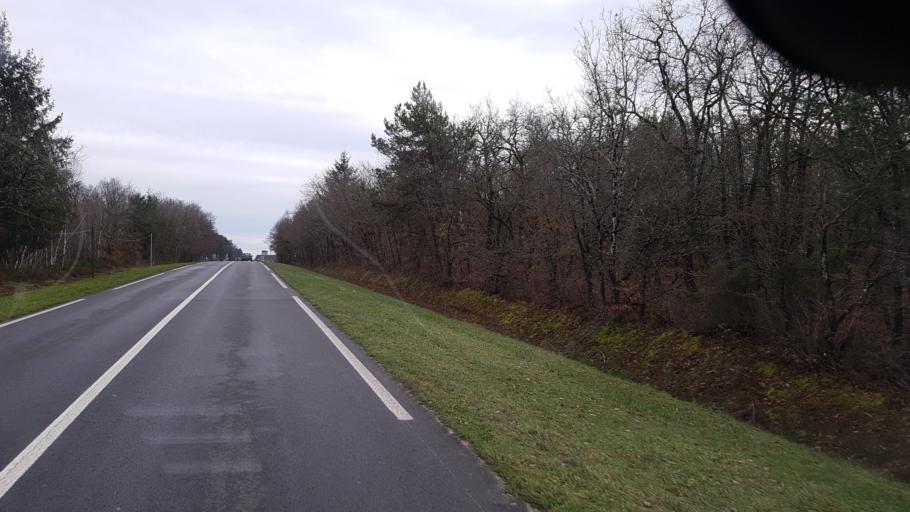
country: FR
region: Centre
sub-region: Departement du Loiret
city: Menestreau-en-Villette
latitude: 47.6494
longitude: 1.9901
